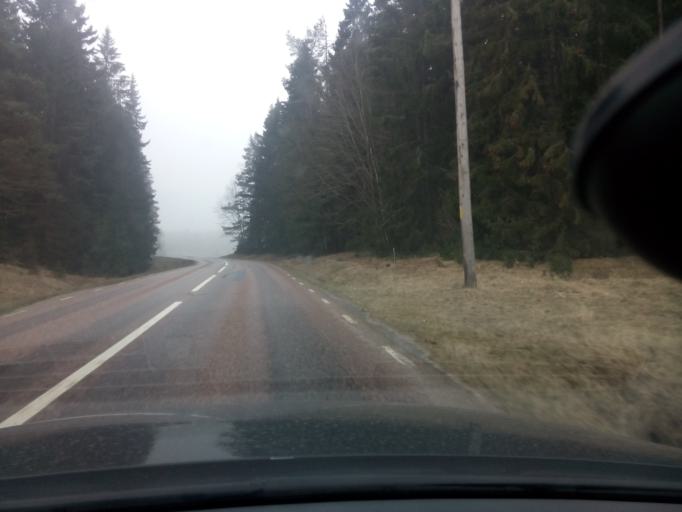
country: SE
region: Soedermanland
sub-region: Nykopings Kommun
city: Nykoping
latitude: 58.8540
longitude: 17.0594
